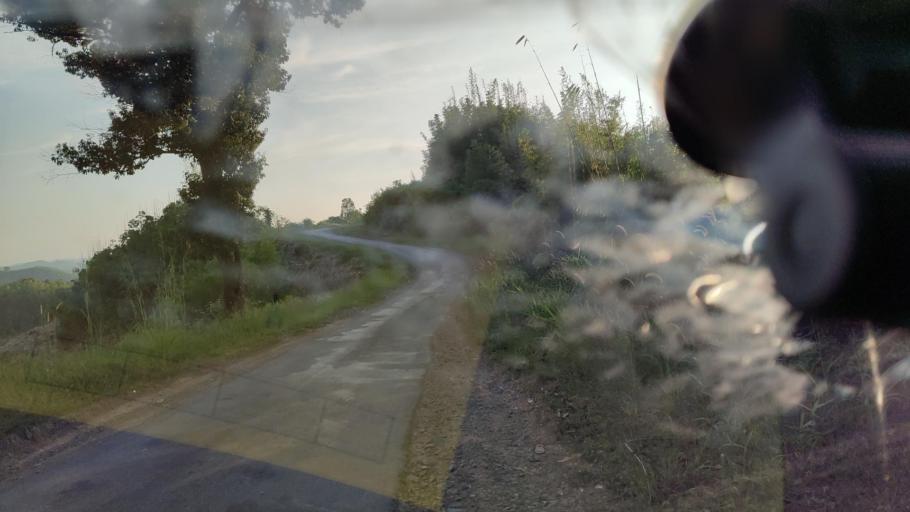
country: MM
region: Magway
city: Minbu
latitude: 19.8476
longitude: 94.1090
